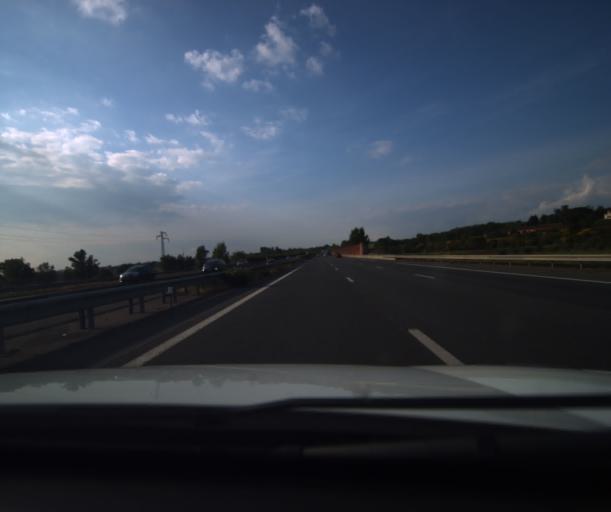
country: FR
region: Midi-Pyrenees
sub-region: Departement de la Haute-Garonne
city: Bouloc
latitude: 43.7701
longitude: 1.3848
